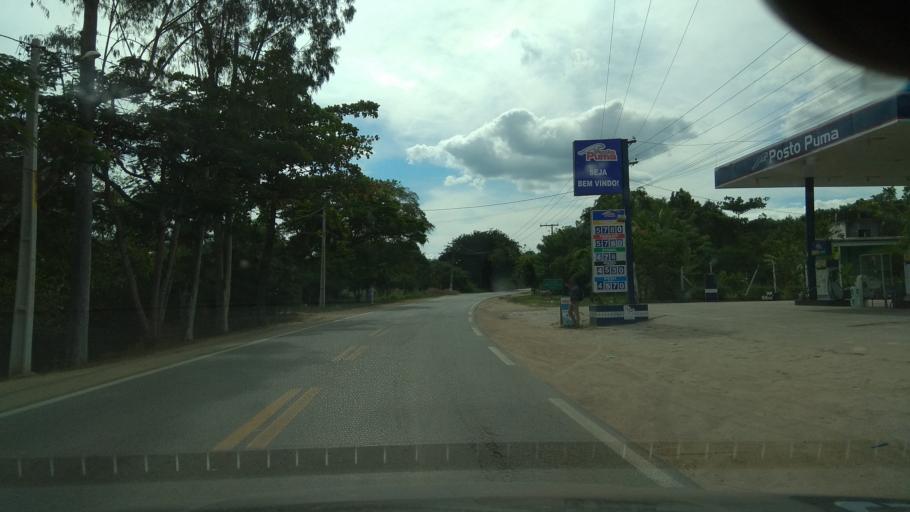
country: BR
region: Bahia
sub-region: Ipiau
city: Ipiau
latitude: -14.1200
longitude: -39.7703
